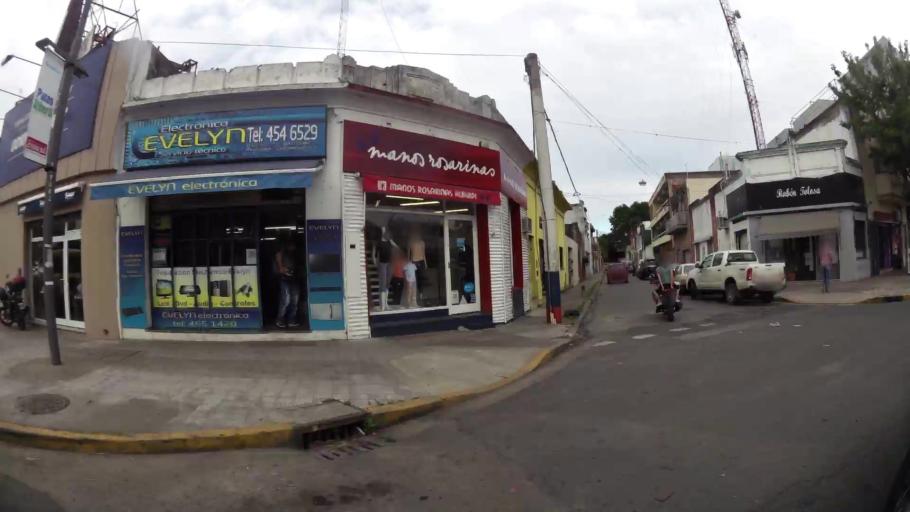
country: AR
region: Santa Fe
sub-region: Departamento de Rosario
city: Rosario
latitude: -32.9145
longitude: -60.6861
